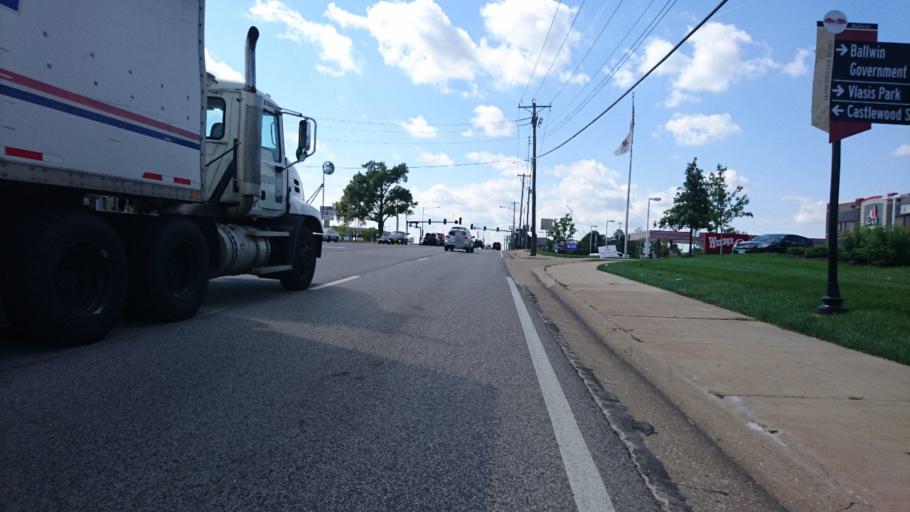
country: US
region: Missouri
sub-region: Saint Louis County
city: Winchester
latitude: 38.5931
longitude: -90.5360
